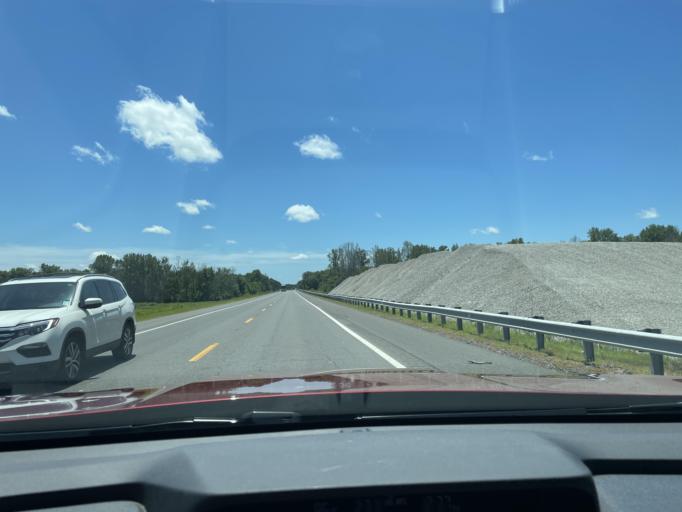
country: US
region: Arkansas
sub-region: Jefferson County
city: Pine Bluff
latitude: 34.1467
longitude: -91.9773
